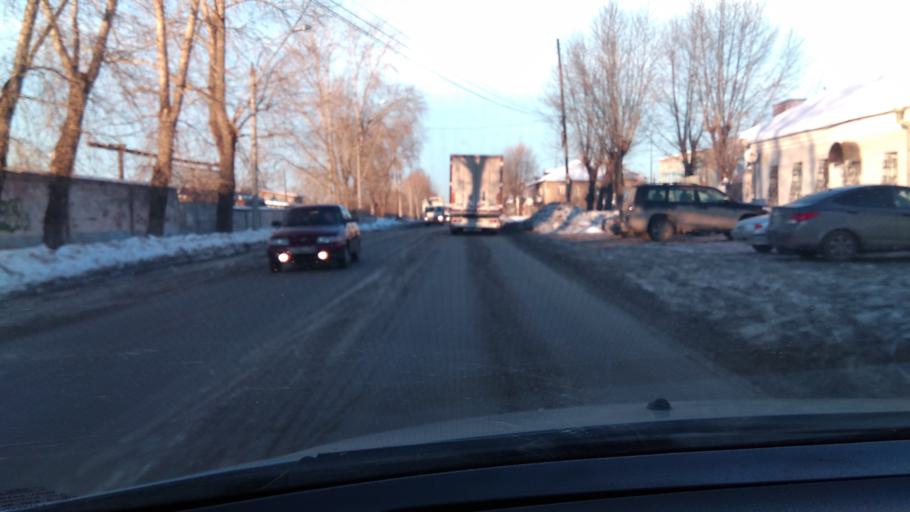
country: RU
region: Sverdlovsk
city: Sovkhoznyy
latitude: 56.7634
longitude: 60.6278
